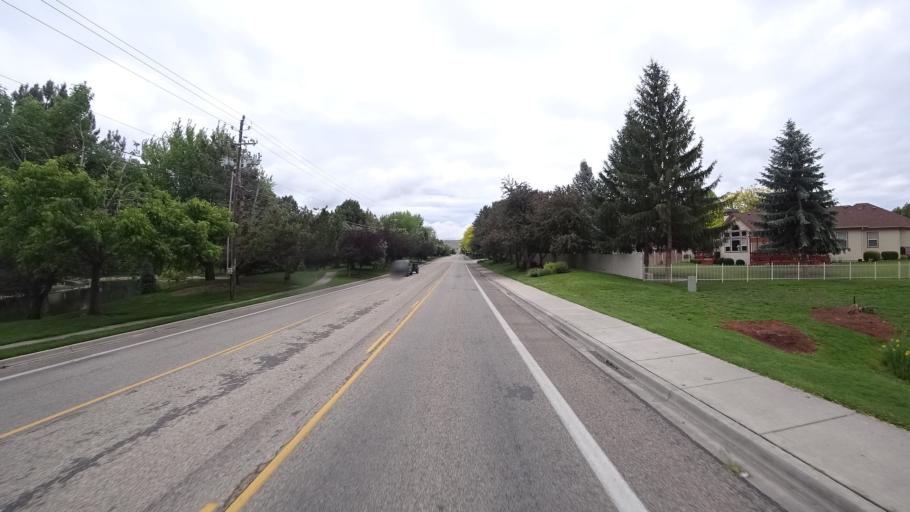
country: US
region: Idaho
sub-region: Ada County
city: Eagle
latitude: 43.7065
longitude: -116.3281
